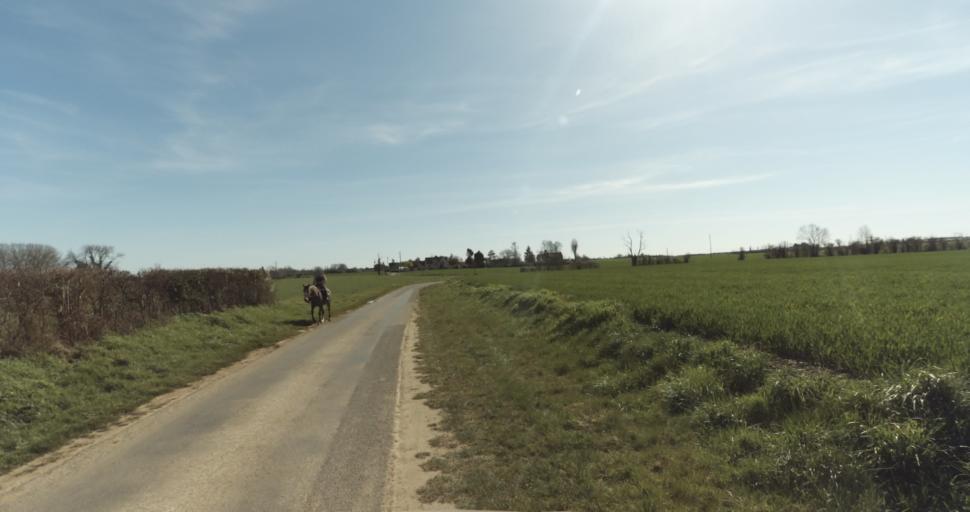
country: FR
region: Lower Normandy
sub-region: Departement du Calvados
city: Saint-Pierre-sur-Dives
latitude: 49.0477
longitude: -0.0265
